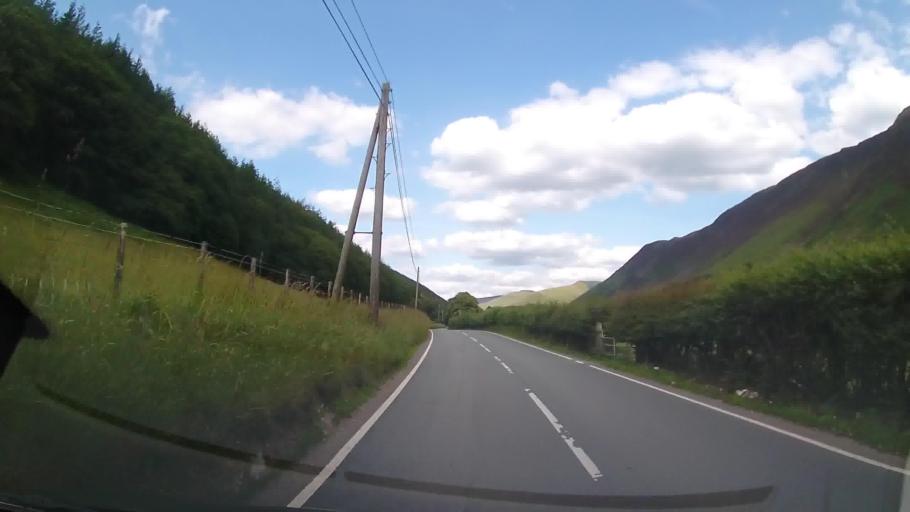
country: GB
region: Wales
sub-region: Gwynedd
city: Corris
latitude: 52.6579
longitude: -3.9301
